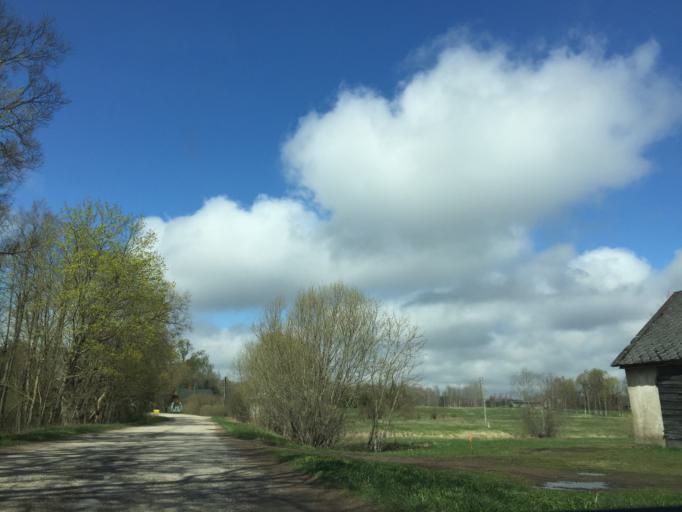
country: LV
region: Apes Novads
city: Ape
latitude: 57.4820
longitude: 26.4442
